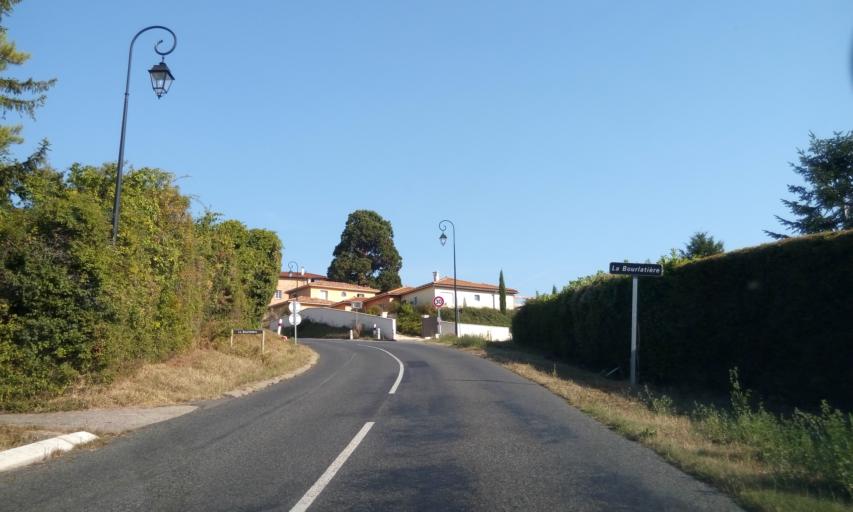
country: FR
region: Rhone-Alpes
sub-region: Departement du Rhone
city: Lucenay
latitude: 45.9260
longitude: 4.6773
